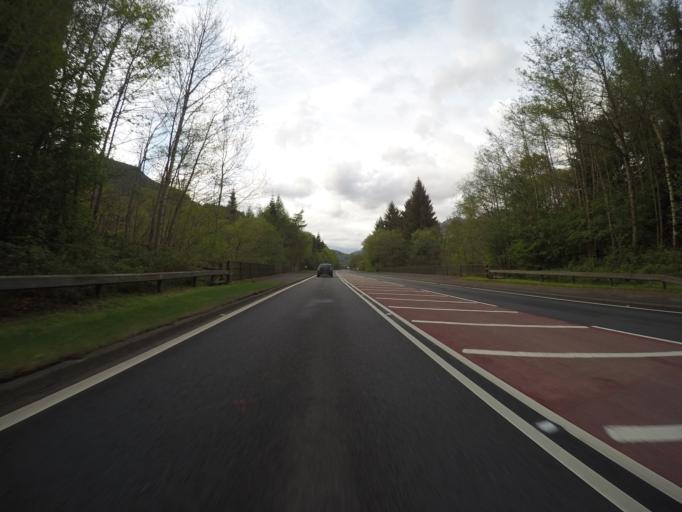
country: GB
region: Scotland
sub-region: Argyll and Bute
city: Helensburgh
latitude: 56.1455
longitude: -4.6643
